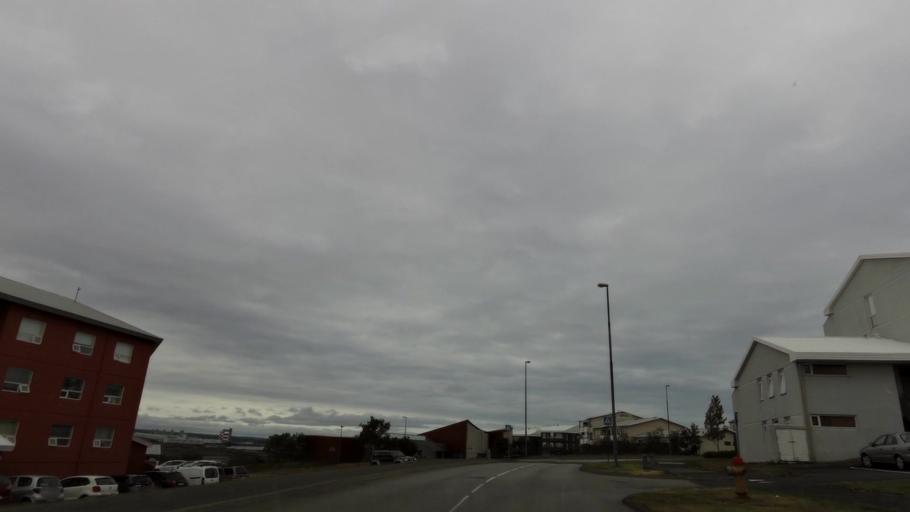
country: IS
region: Capital Region
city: Hafnarfjoerdur
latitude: 64.0557
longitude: -21.9807
